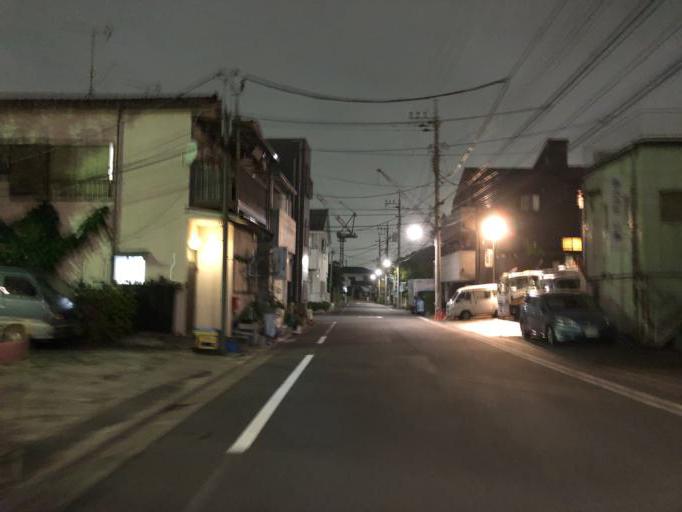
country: JP
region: Tokyo
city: Urayasu
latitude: 35.6698
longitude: 139.8728
